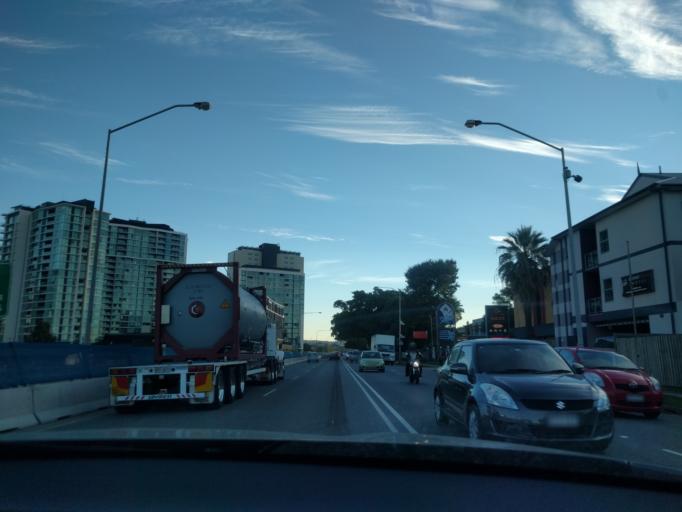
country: AU
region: Queensland
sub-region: Brisbane
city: Ascot
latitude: -27.4380
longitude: 153.0691
